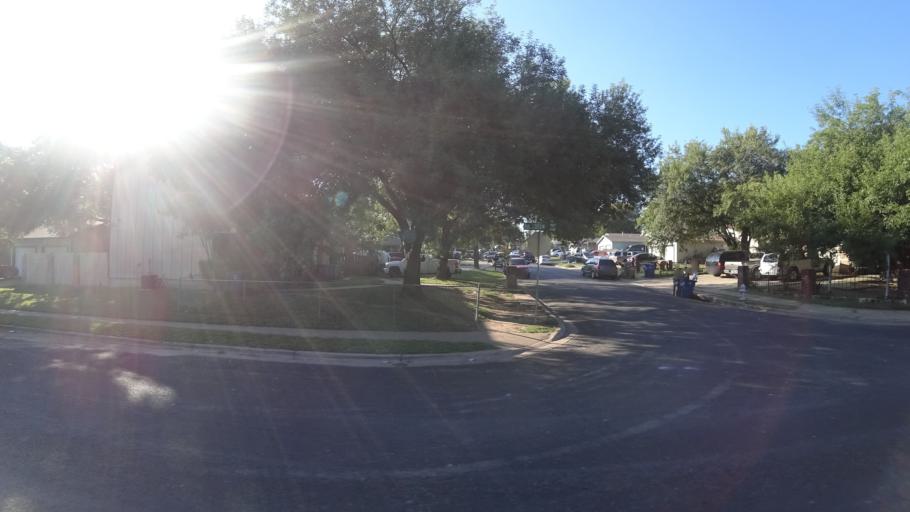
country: US
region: Texas
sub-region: Travis County
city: Wells Branch
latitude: 30.3566
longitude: -97.6763
